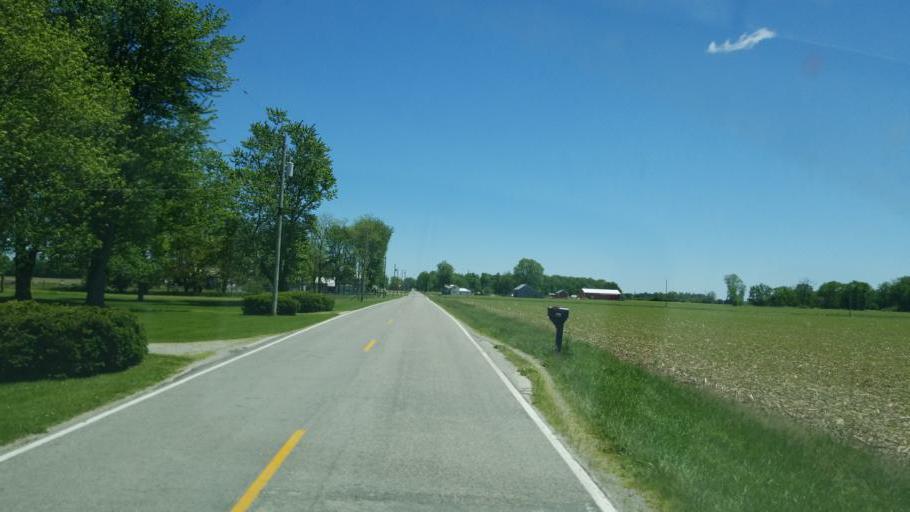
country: US
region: Indiana
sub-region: Randolph County
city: Union City
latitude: 40.2816
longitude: -84.7689
